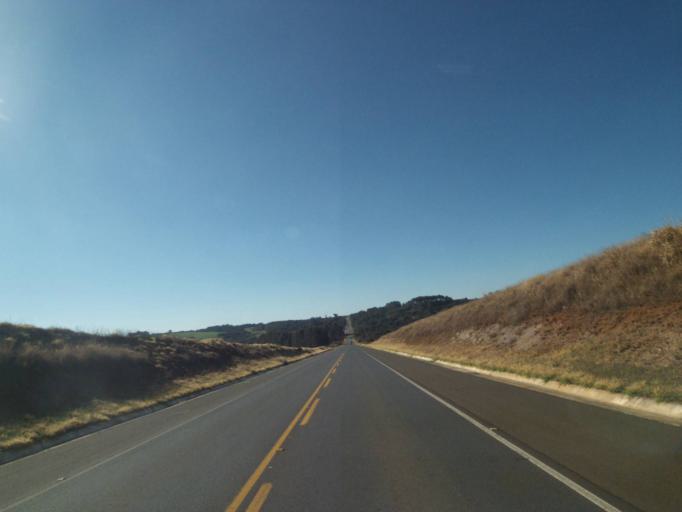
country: BR
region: Parana
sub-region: Tibagi
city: Tibagi
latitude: -24.6168
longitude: -50.4477
